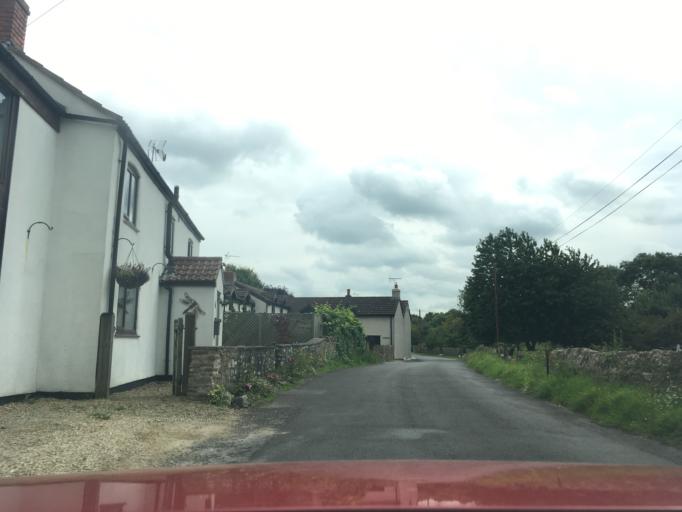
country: GB
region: England
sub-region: South Gloucestershire
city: Tytherington
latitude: 51.5980
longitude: -2.5003
